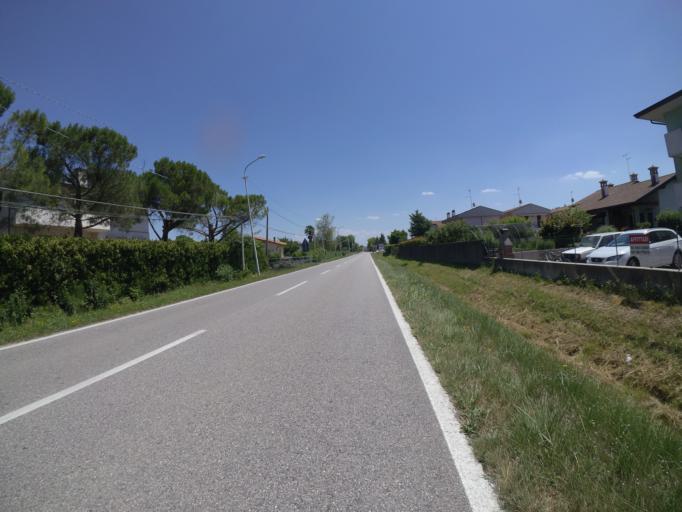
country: IT
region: Friuli Venezia Giulia
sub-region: Provincia di Udine
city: Rivignano
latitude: 45.8789
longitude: 13.0337
